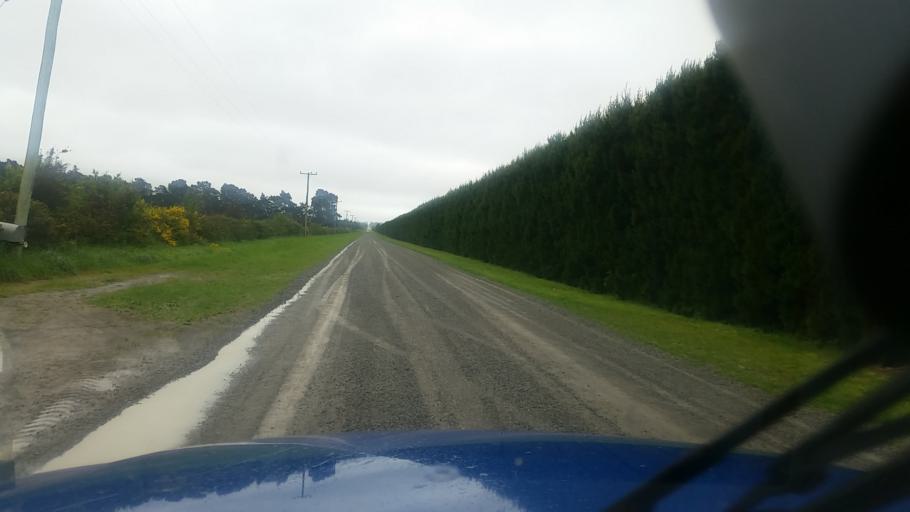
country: NZ
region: Canterbury
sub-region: Ashburton District
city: Methven
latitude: -43.5893
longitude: 171.7000
